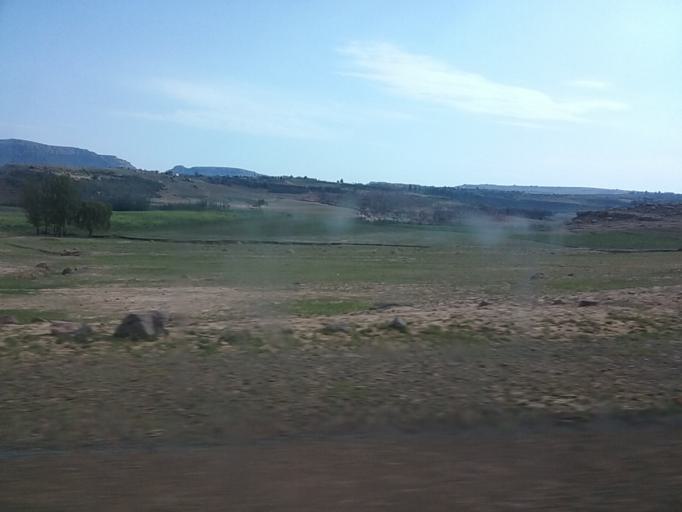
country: LS
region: Berea
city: Teyateyaneng
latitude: -29.0853
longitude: 27.9152
